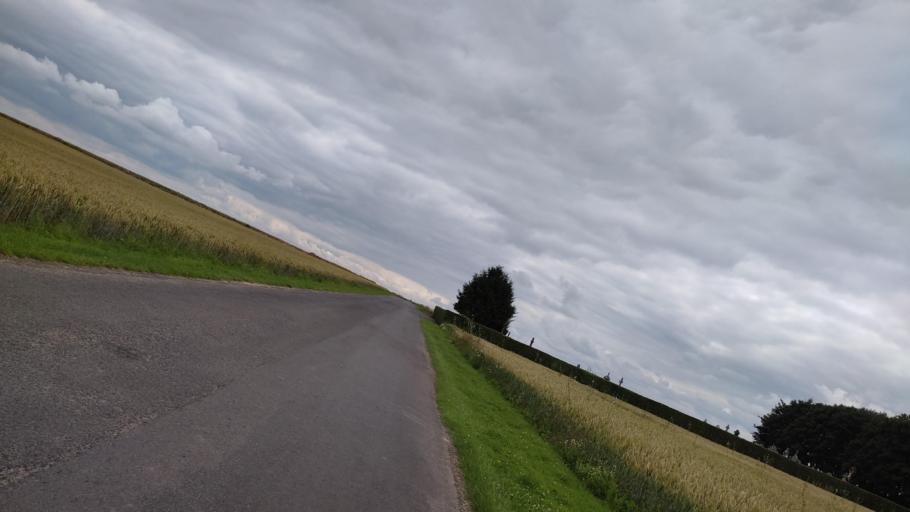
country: FR
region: Nord-Pas-de-Calais
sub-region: Departement du Pas-de-Calais
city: Beaumetz-les-Loges
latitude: 50.2352
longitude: 2.6302
